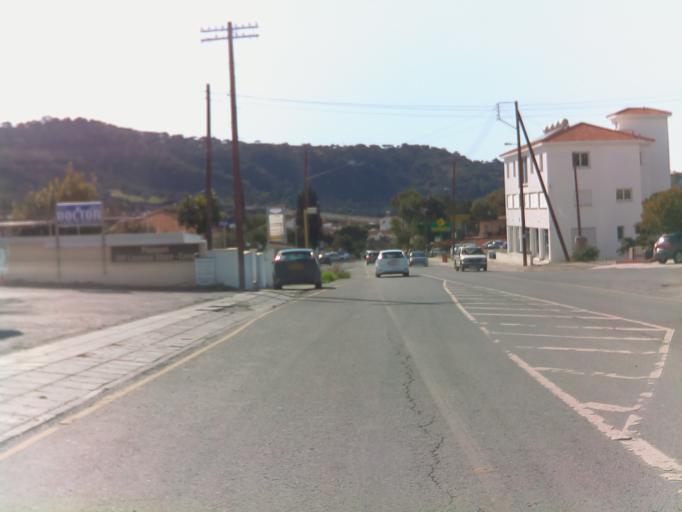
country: CY
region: Limassol
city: Pissouri
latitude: 34.6761
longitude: 32.6986
